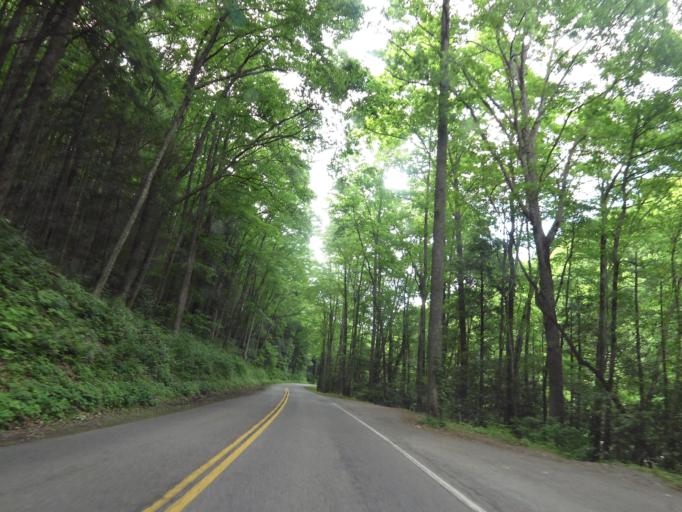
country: US
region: Tennessee
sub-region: Sevier County
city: Gatlinburg
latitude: 35.6693
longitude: -83.6375
